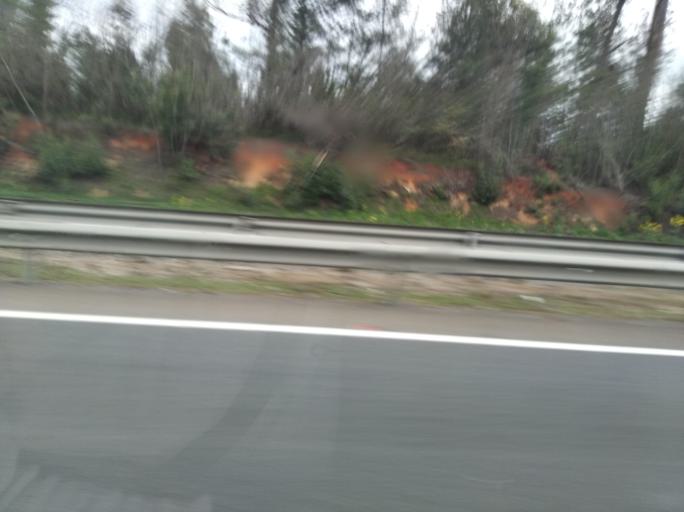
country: CL
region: Valparaiso
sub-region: Provincia de Valparaiso
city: Vina del Mar
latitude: -33.1577
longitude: -71.5490
